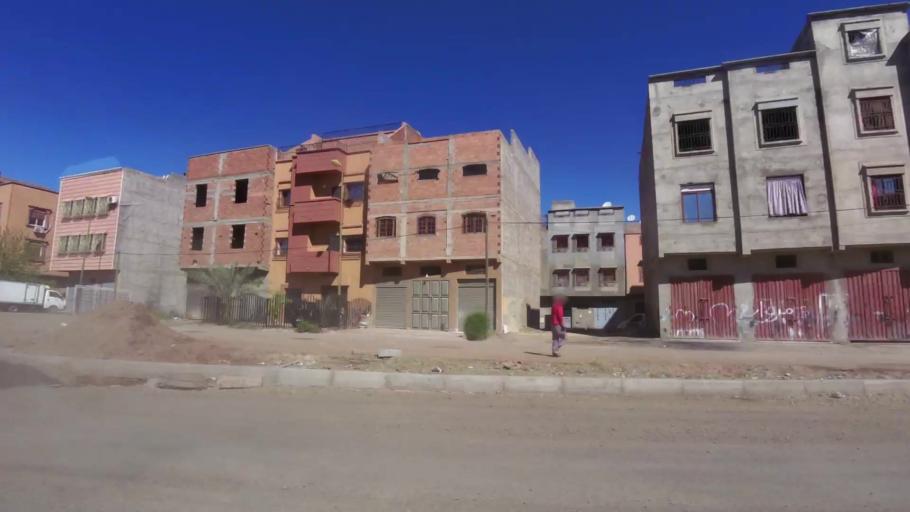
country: MA
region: Marrakech-Tensift-Al Haouz
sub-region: Marrakech
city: Marrakesh
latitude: 31.5926
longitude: -8.0551
